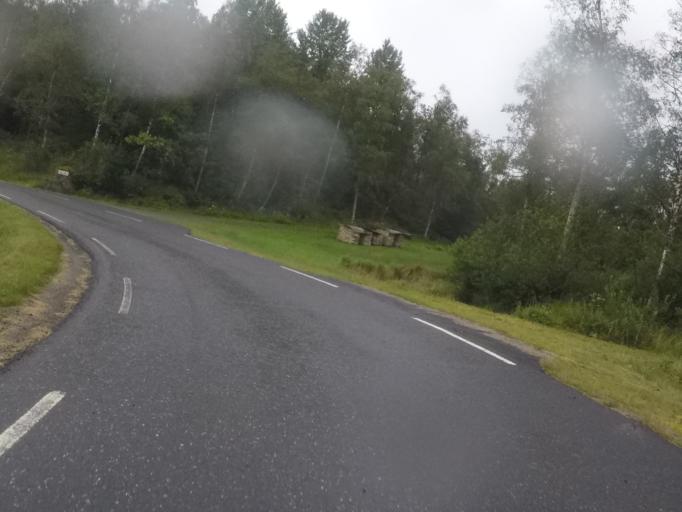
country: NO
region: Vest-Agder
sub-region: Lyngdal
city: Lyngdal
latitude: 58.2532
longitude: 7.0647
